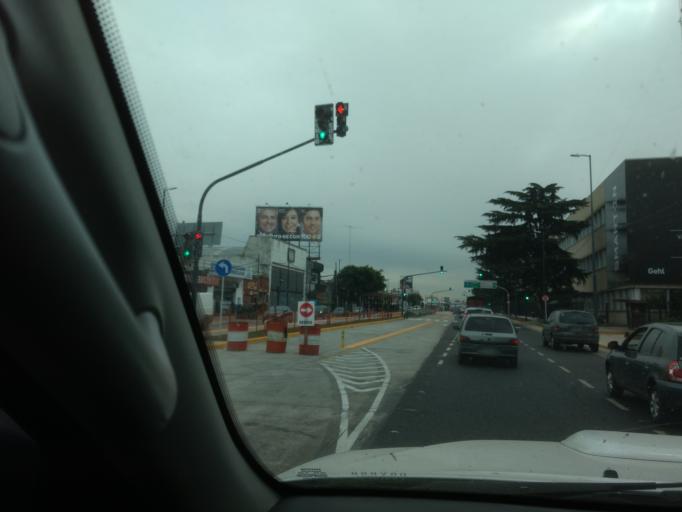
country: AR
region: Buenos Aires
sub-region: Partido de General San Martin
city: General San Martin
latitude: -34.5882
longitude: -58.5222
